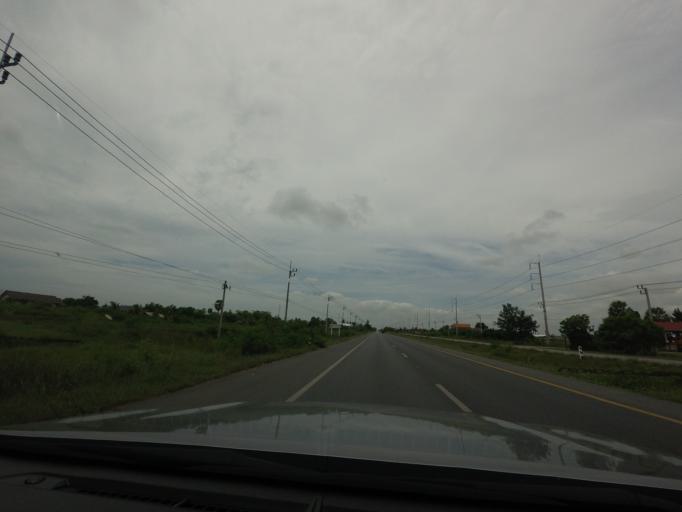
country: TH
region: Nakhon Si Thammarat
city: Hua Sai
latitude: 8.0369
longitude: 100.2893
